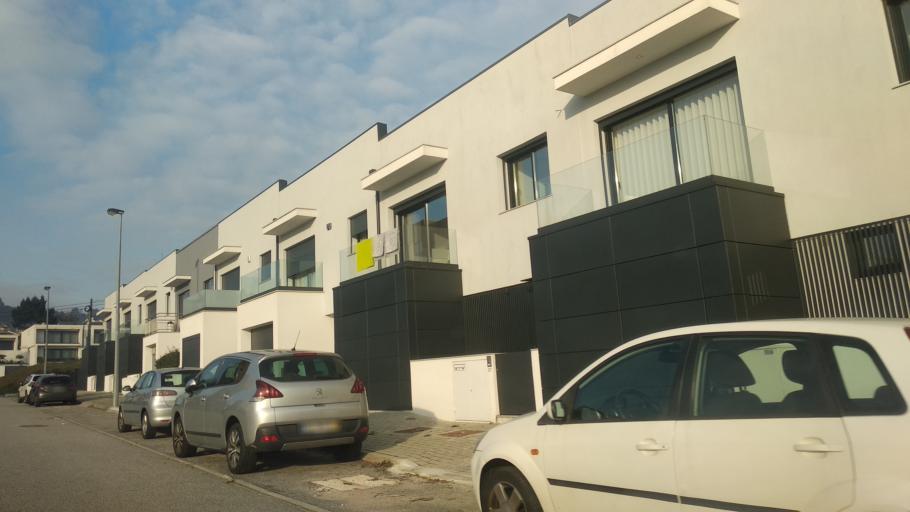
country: PT
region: Braga
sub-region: Braga
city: Adaufe
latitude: 41.5654
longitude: -8.3816
